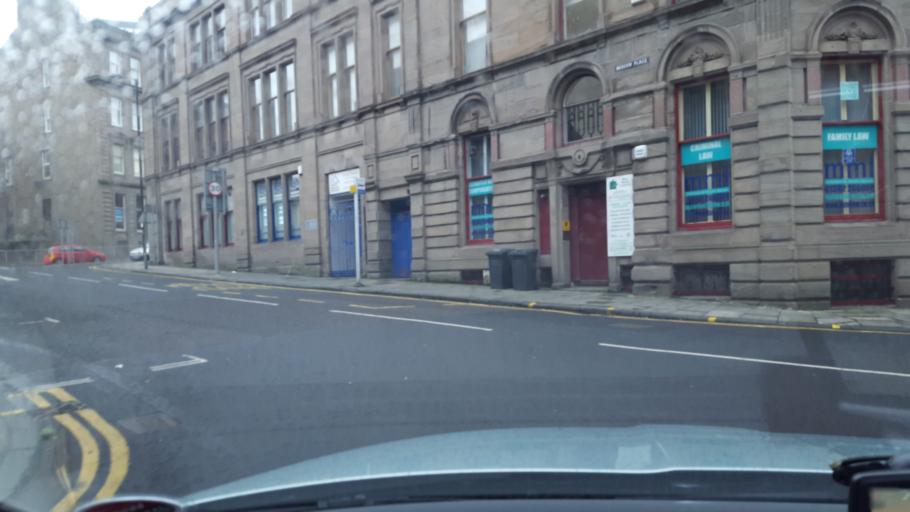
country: GB
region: Scotland
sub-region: Dundee City
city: Dundee
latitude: 56.4635
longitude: -2.9714
